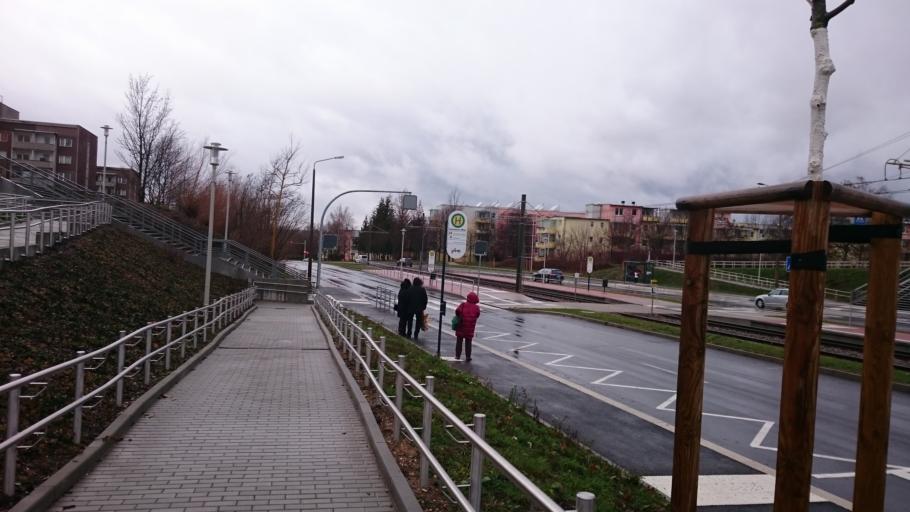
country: DE
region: Saxony
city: Zwickau
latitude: 50.7326
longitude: 12.5207
